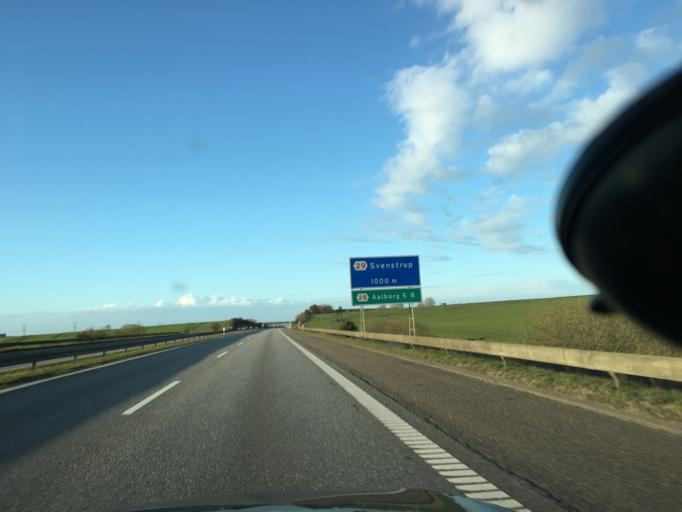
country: DK
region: North Denmark
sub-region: Alborg Kommune
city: Svenstrup
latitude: 56.9355
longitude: 9.8528
